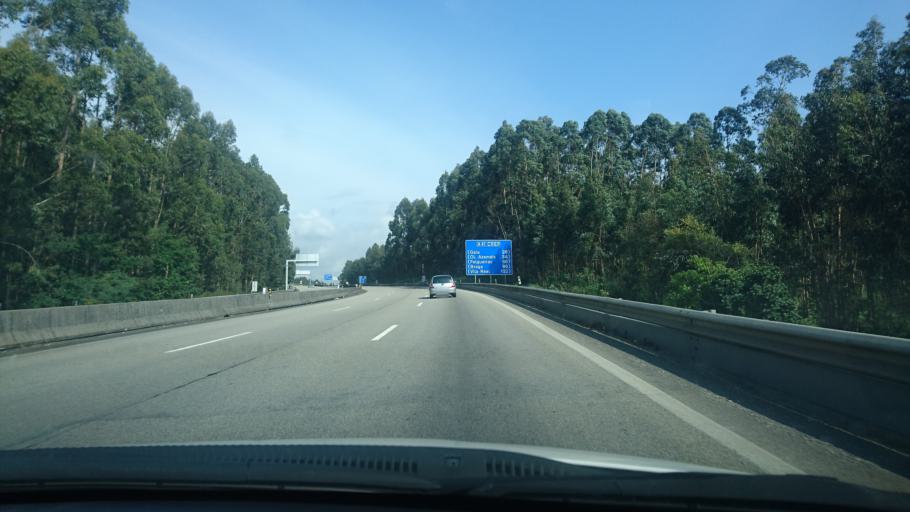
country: PT
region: Porto
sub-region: Vila Nova de Gaia
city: Grijo
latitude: 41.0102
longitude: -8.5665
